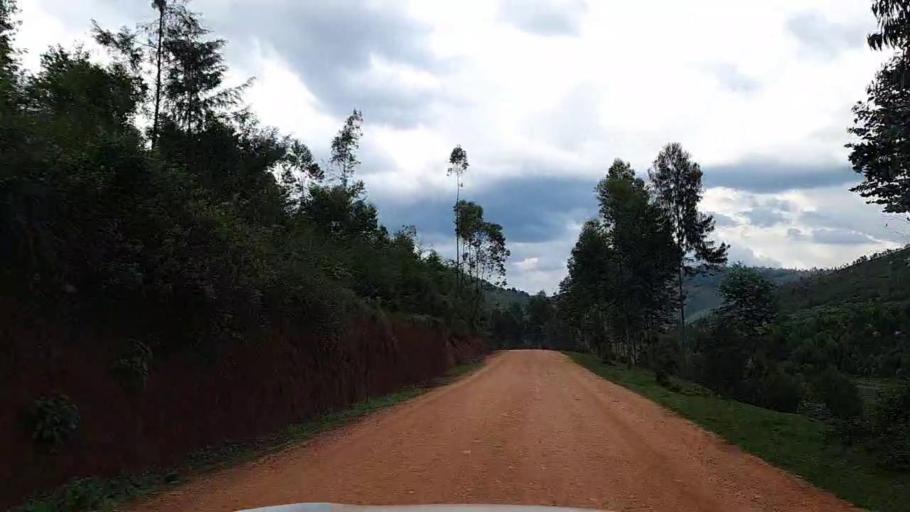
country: RW
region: Southern Province
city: Nyanza
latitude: -2.4034
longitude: 29.6766
